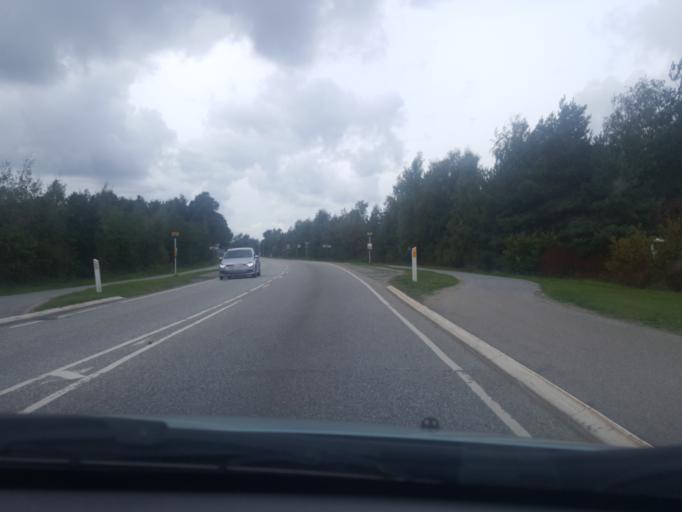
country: DK
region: Zealand
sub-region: Guldborgsund Kommune
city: Nykobing Falster
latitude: 54.6966
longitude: 11.9565
